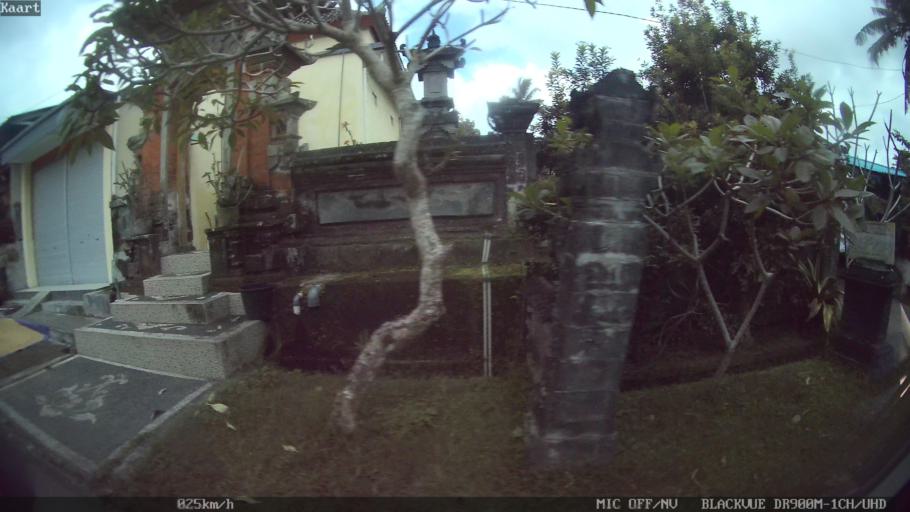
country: ID
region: Bali
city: Banjar Susut Kaja
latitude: -8.4437
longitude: 115.3392
